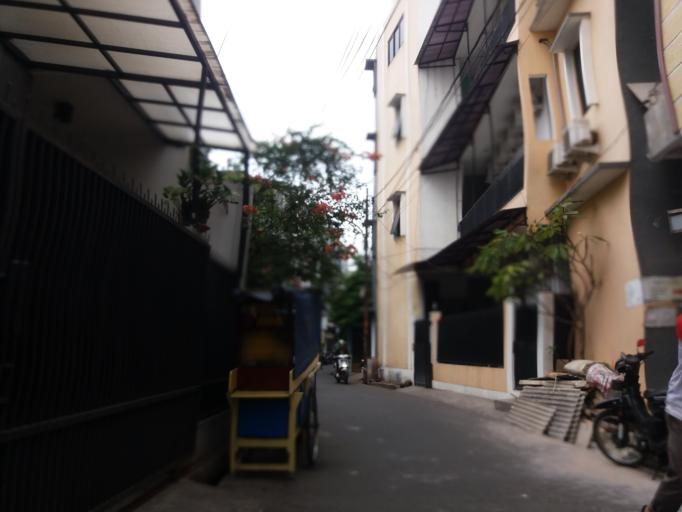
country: ID
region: Jakarta Raya
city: Jakarta
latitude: -6.2142
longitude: 106.8234
